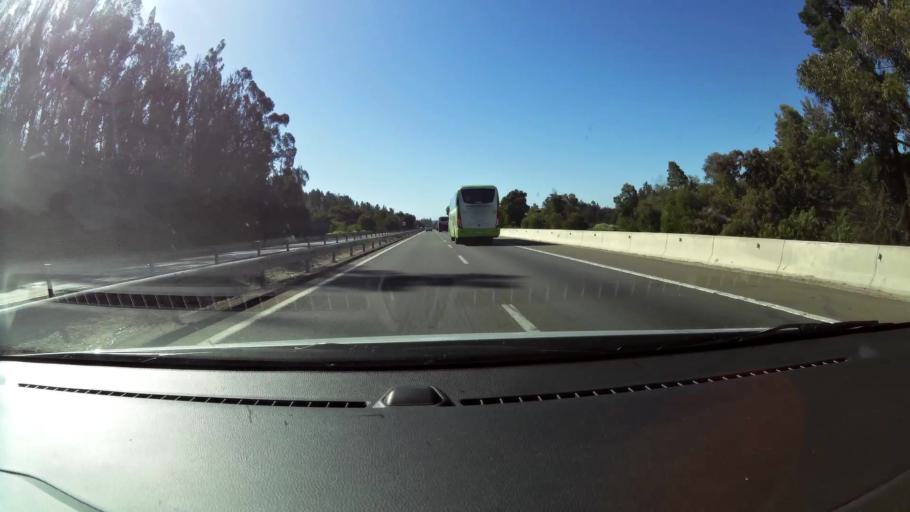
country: CL
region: Valparaiso
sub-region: Provincia de Marga Marga
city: Quilpue
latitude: -33.1887
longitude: -71.4992
